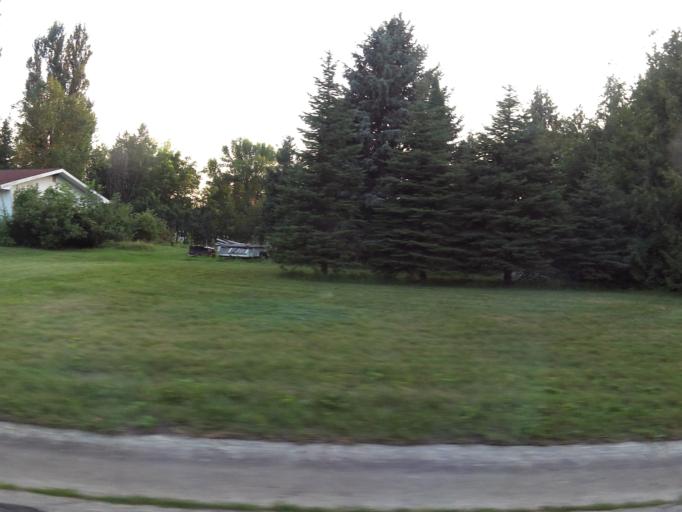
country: US
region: North Dakota
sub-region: Grand Forks County
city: Grand Forks
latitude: 47.8567
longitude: -97.0097
